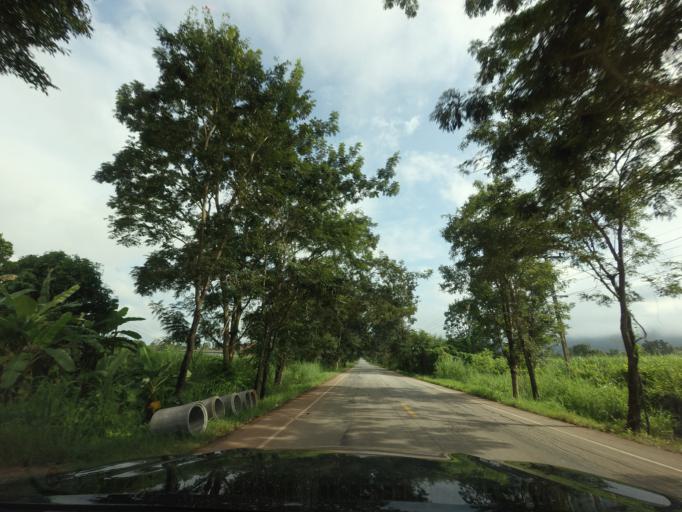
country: TH
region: Changwat Udon Thani
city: Nam Som
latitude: 17.8466
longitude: 102.2561
